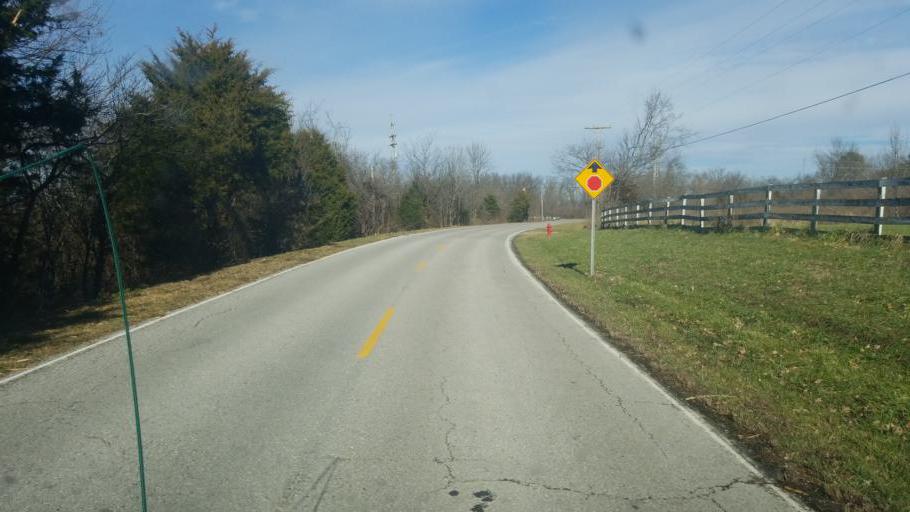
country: US
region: Illinois
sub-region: Jackson County
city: Carbondale
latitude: 37.6986
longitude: -89.2122
